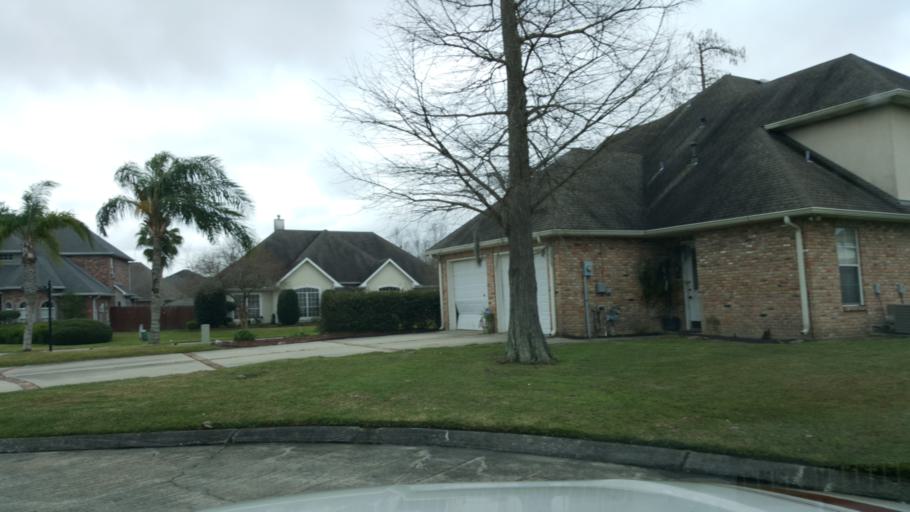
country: US
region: Louisiana
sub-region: Jefferson Parish
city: Woodmere
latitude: 29.8770
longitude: -90.0814
